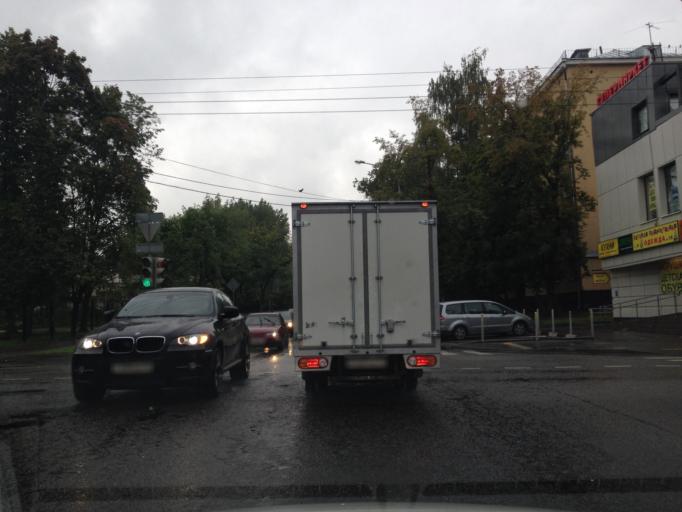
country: RU
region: Moskovskaya
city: Izmaylovo
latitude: 55.7971
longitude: 37.8125
